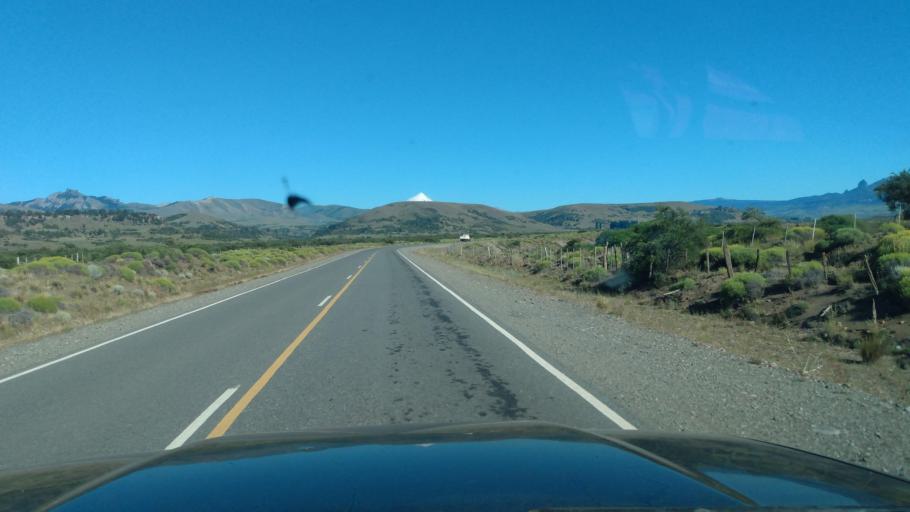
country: AR
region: Neuquen
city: Junin de los Andes
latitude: -39.8737
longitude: -71.1730
